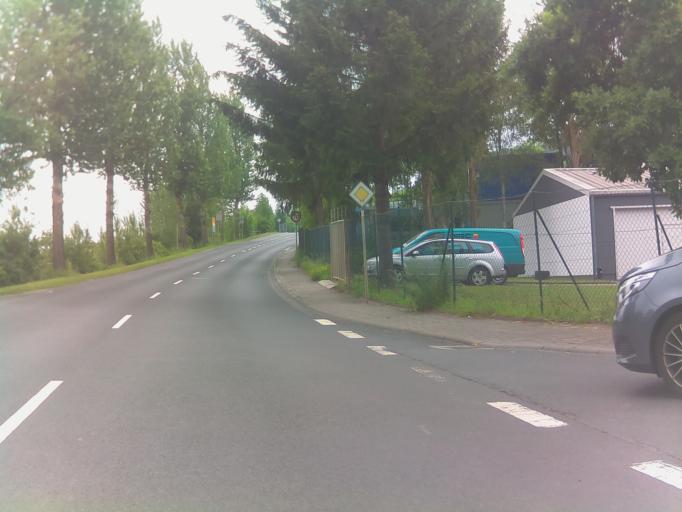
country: DE
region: Hesse
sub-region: Regierungsbezirk Kassel
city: Grossenluder
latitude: 50.5551
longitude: 9.6033
